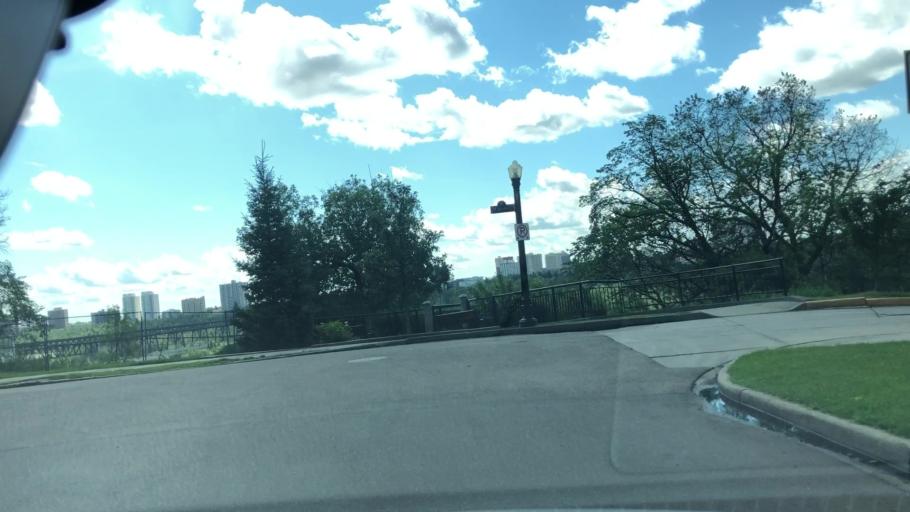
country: CA
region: Alberta
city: Edmonton
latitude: 53.5375
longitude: -113.5176
